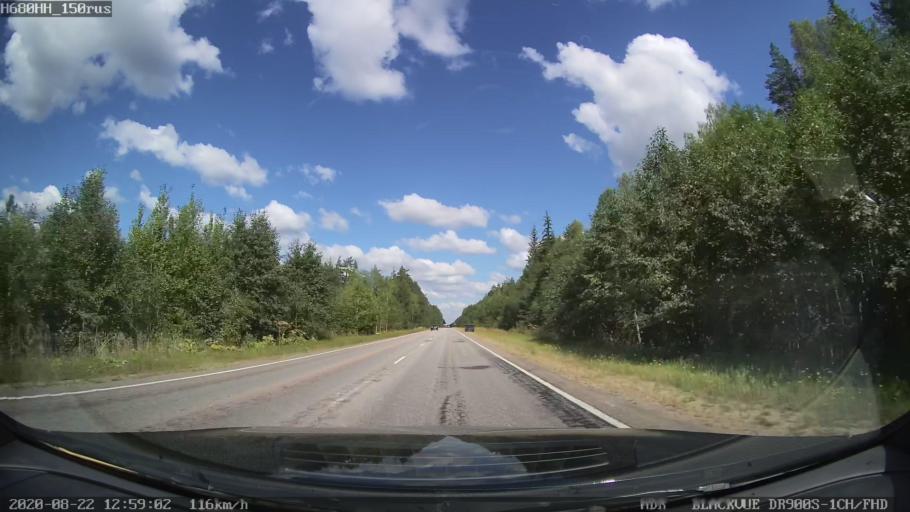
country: RU
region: Tverskaya
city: Bezhetsk
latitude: 57.5994
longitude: 36.3539
